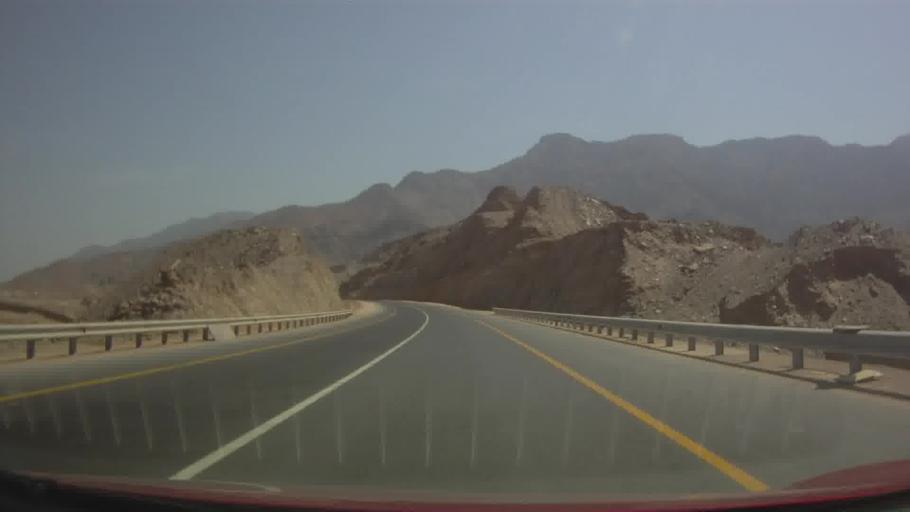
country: OM
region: Muhafazat Masqat
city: Muscat
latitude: 23.4000
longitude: 58.7818
